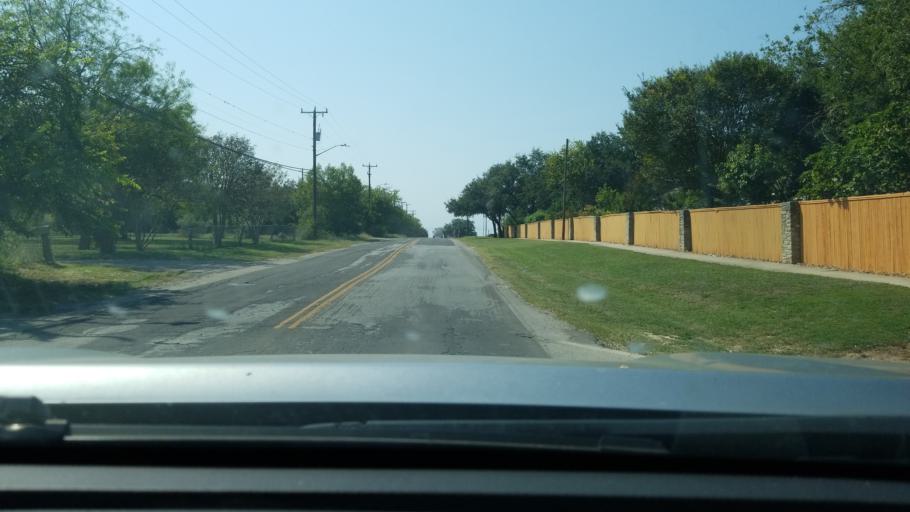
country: US
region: Texas
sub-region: Bexar County
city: Leon Valley
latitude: 29.5447
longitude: -98.6099
